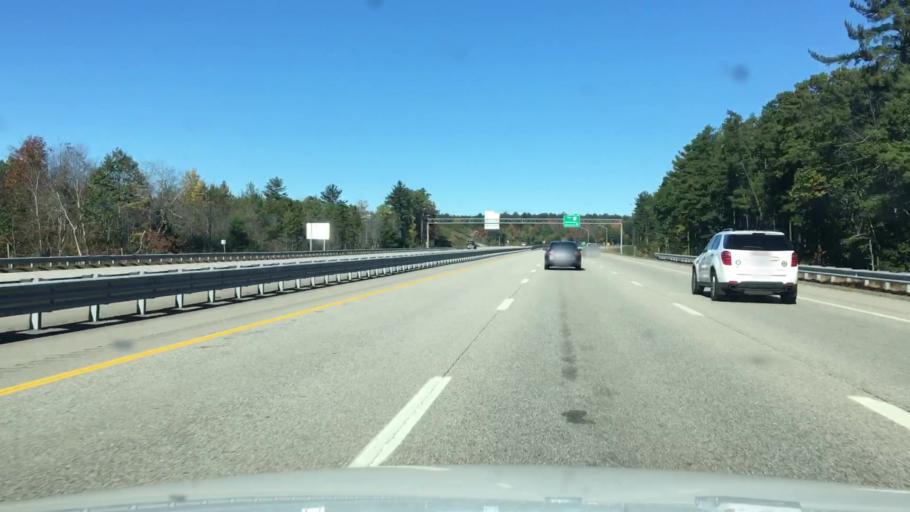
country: US
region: New Hampshire
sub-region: Strafford County
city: Rochester
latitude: 43.2900
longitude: -70.9889
